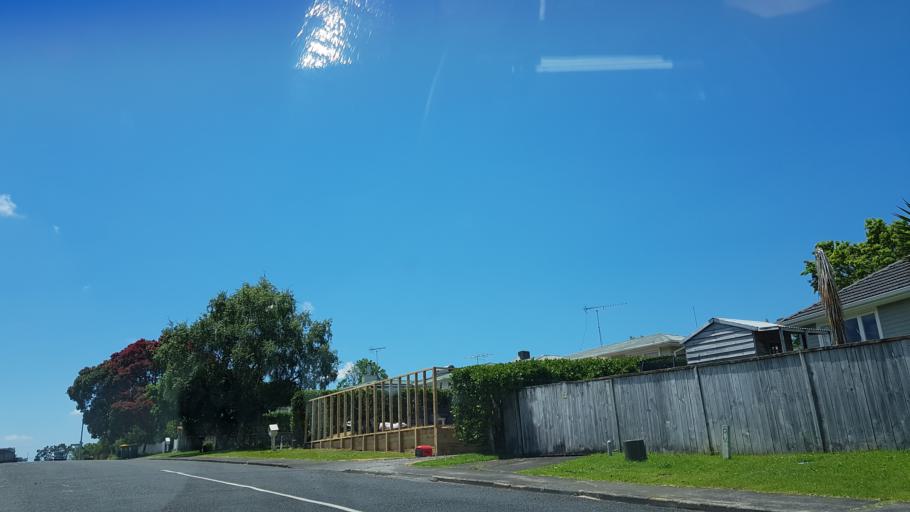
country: NZ
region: Auckland
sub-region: Auckland
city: North Shore
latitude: -36.7877
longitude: 174.6918
